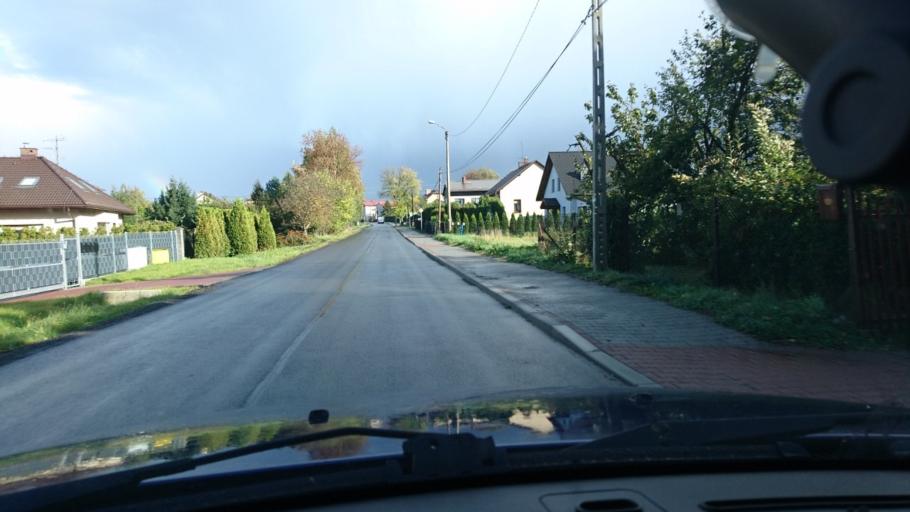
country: PL
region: Silesian Voivodeship
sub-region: Powiat bielski
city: Mazancowice
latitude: 49.8591
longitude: 19.0028
